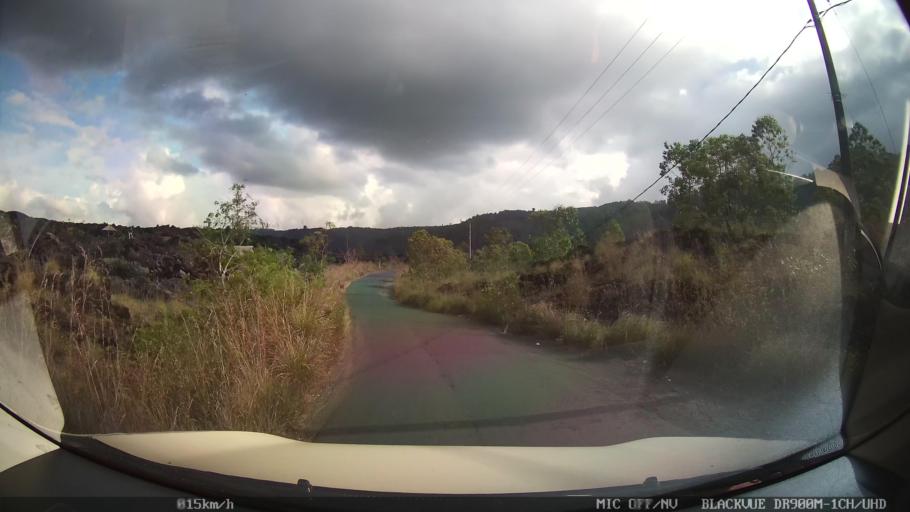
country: ID
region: Bali
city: Banjar Kedisan
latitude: -8.2393
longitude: 115.3526
